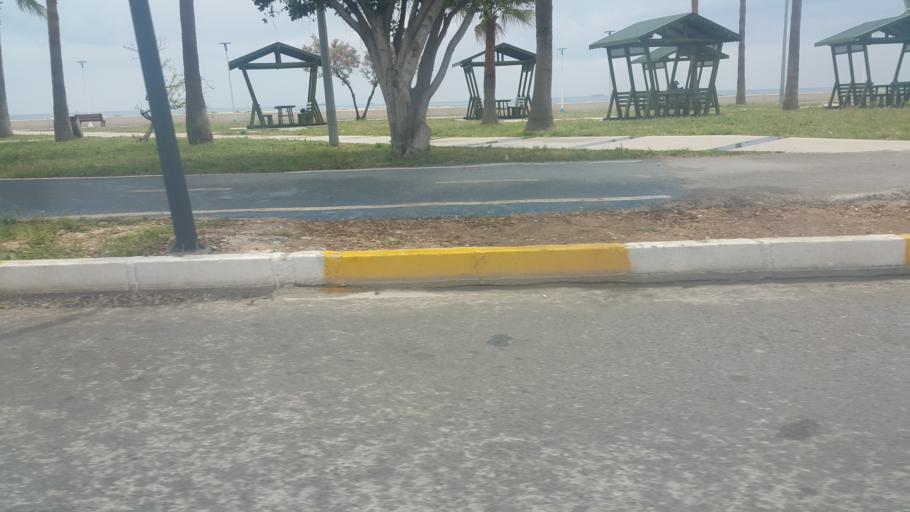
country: TR
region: Mersin
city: Mercin
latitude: 36.7639
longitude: 34.5558
